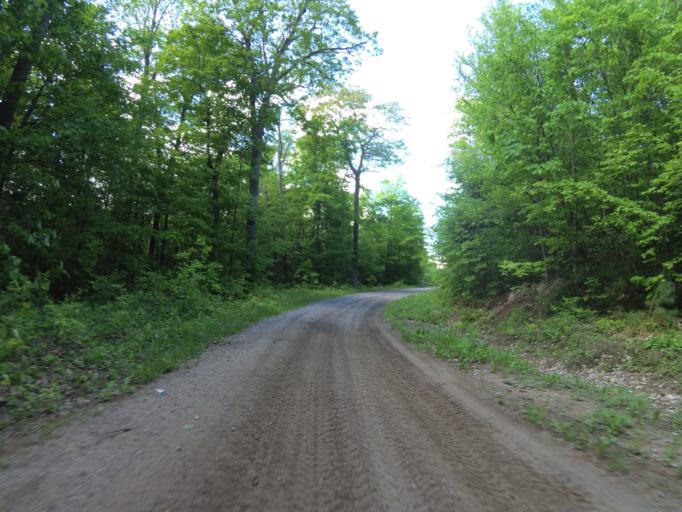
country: CA
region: Ontario
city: Renfrew
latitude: 45.1251
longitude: -76.8800
